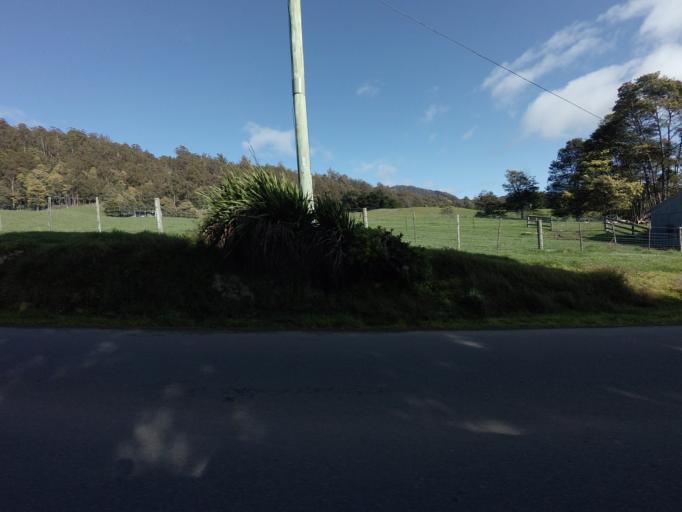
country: AU
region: Tasmania
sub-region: Huon Valley
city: Geeveston
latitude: -43.2435
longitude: 146.9913
